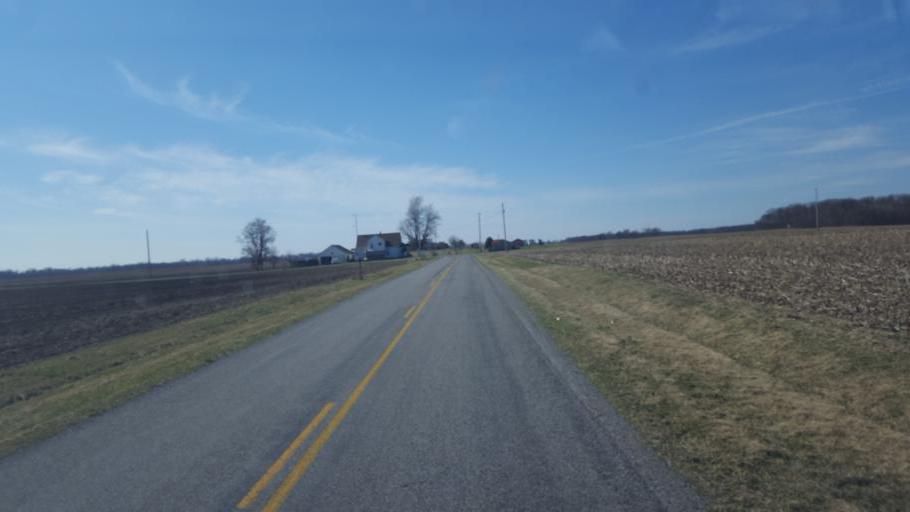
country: US
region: Ohio
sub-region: Union County
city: Richwood
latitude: 40.5144
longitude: -83.4503
